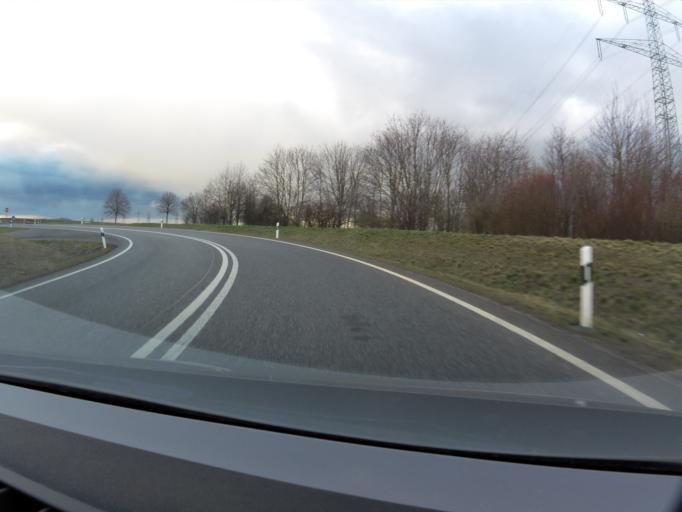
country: DE
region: Thuringia
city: Alkersleben
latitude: 50.8529
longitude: 11.0110
